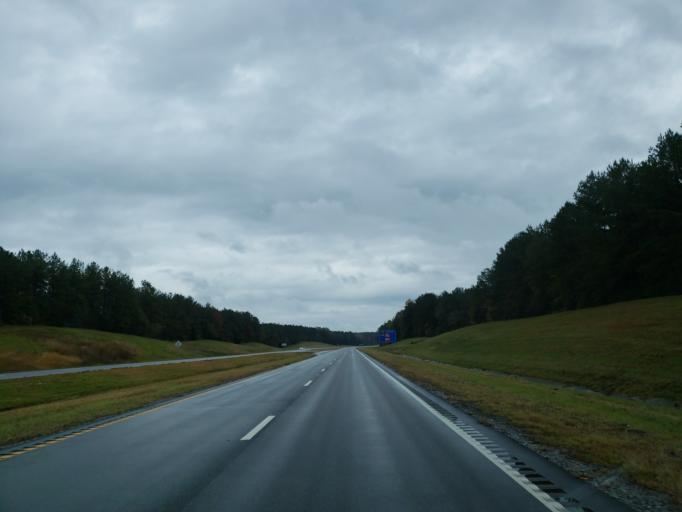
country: US
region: Mississippi
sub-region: Wayne County
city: Waynesboro
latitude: 31.6967
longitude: -88.6596
